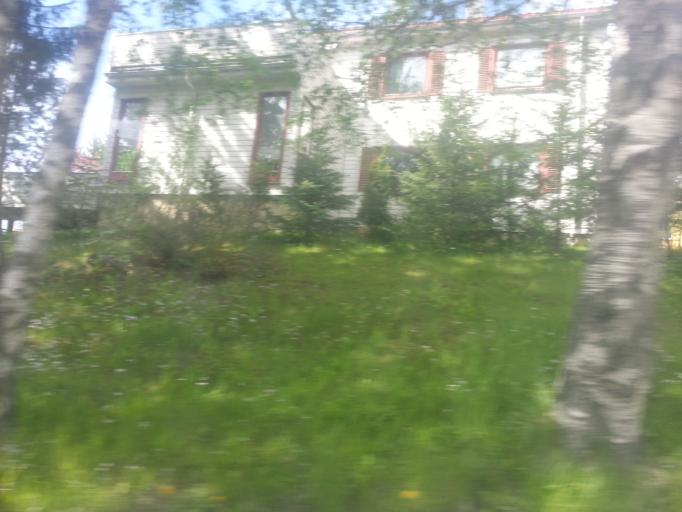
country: NO
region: Sor-Trondelag
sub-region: Trondheim
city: Trondheim
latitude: 63.4161
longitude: 10.4254
